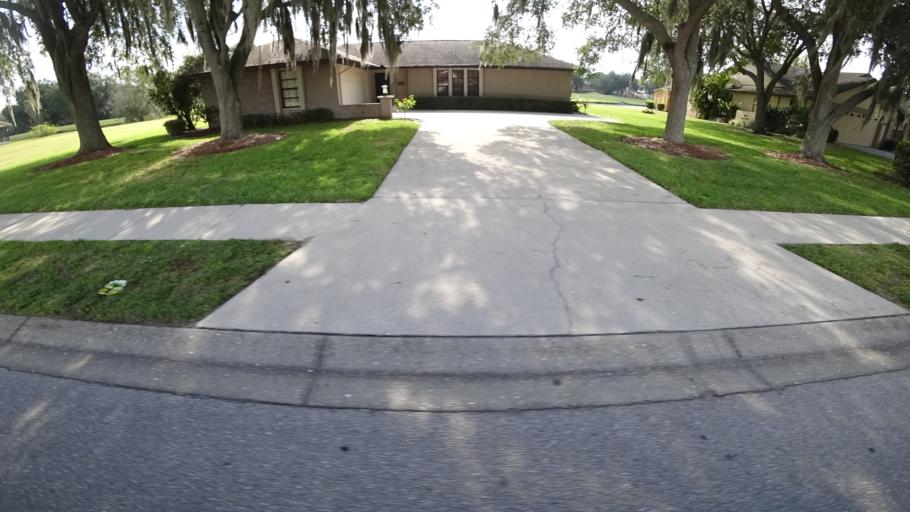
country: US
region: Florida
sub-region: Sarasota County
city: The Meadows
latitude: 27.4303
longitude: -82.4425
